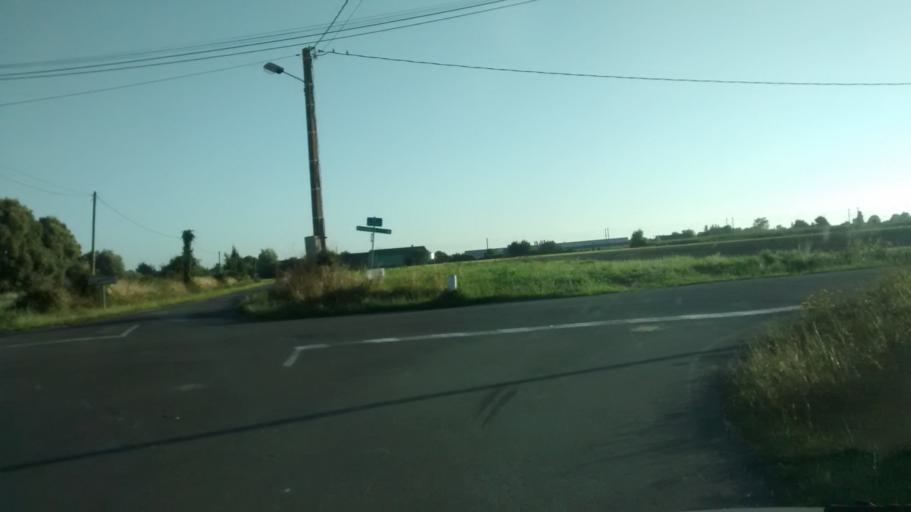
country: FR
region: Brittany
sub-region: Departement d'Ille-et-Vilaine
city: La Fresnais
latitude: 48.5950
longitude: -1.8563
